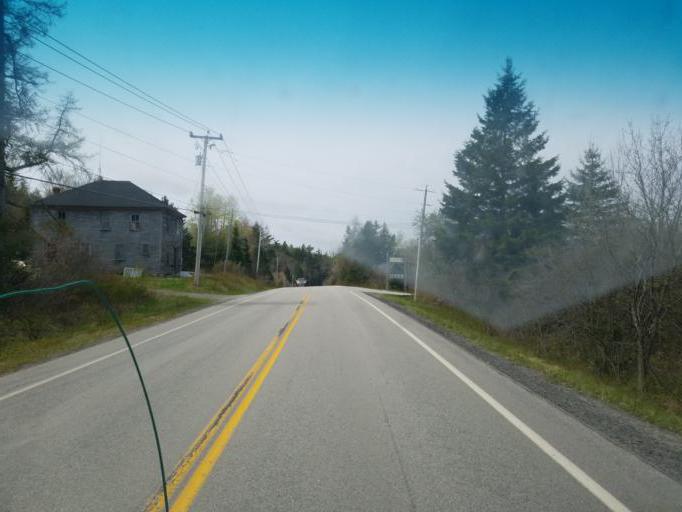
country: US
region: Maine
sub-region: Washington County
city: Eastport
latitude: 44.7989
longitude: -67.1437
